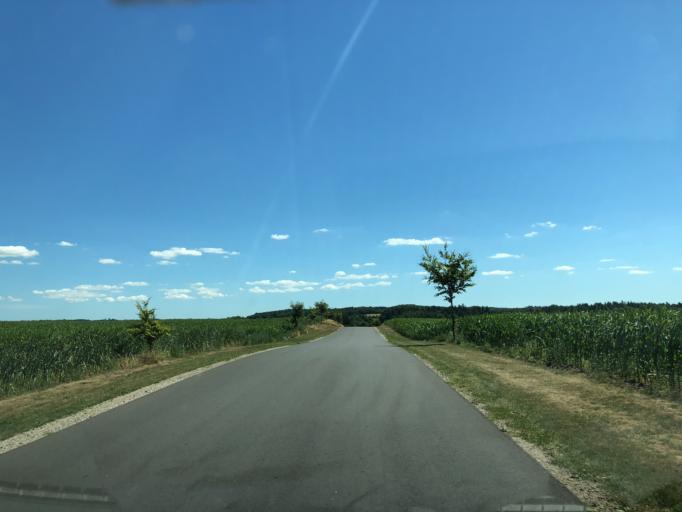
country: DK
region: Central Jutland
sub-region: Viborg Kommune
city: Bjerringbro
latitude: 56.5113
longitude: 9.5693
